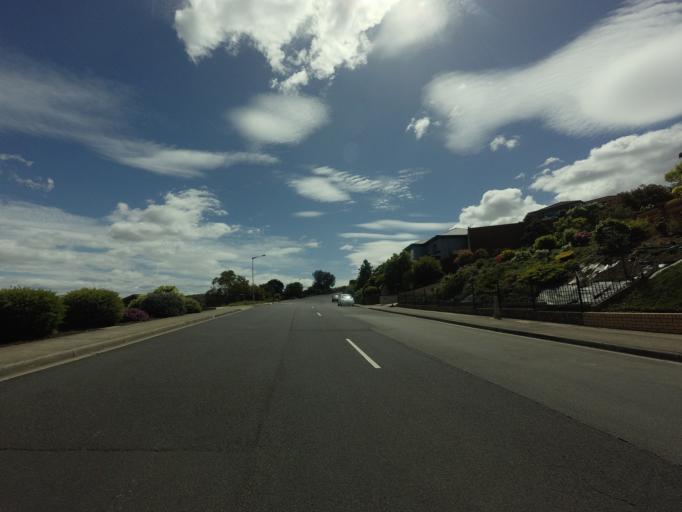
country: AU
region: Tasmania
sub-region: Clarence
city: Howrah
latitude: -42.8897
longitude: 147.4118
